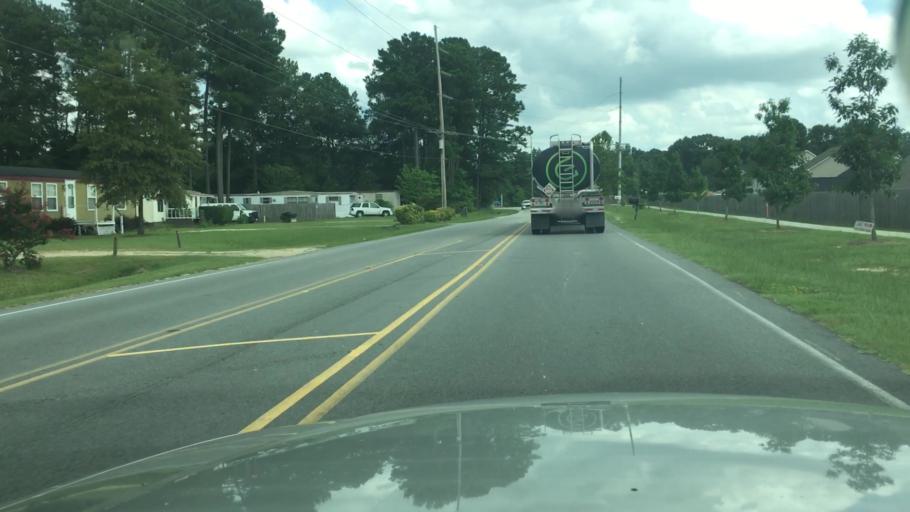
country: US
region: North Carolina
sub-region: Hoke County
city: Rockfish
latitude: 35.0101
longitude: -79.0029
